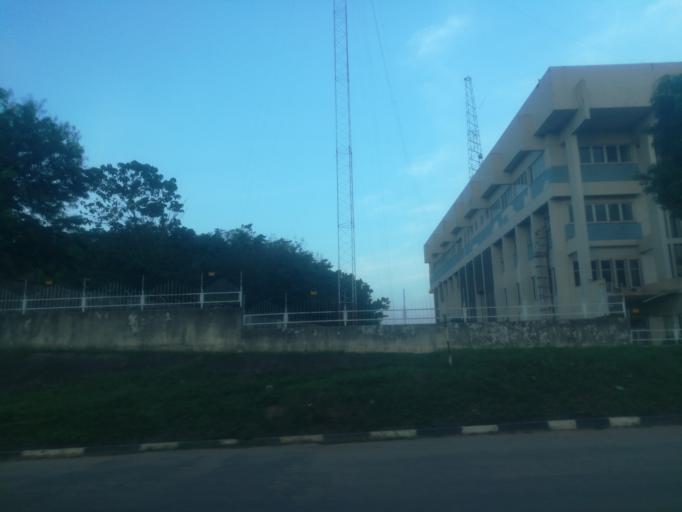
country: NG
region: Ogun
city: Abeokuta
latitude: 7.1388
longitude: 3.3414
